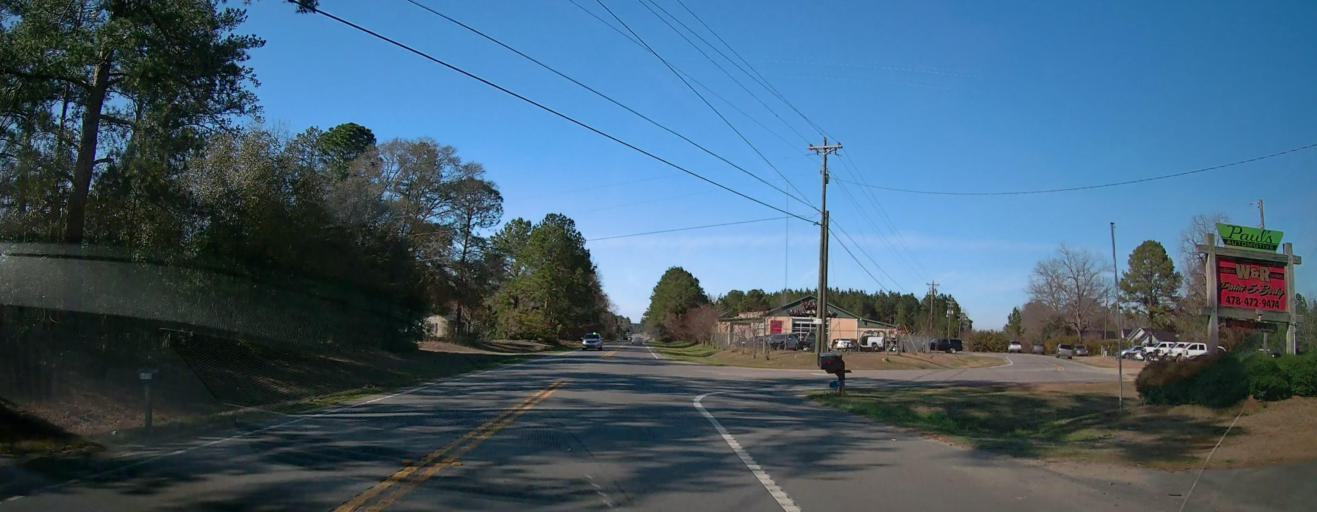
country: US
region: Georgia
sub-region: Macon County
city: Oglethorpe
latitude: 32.3167
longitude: -84.0656
